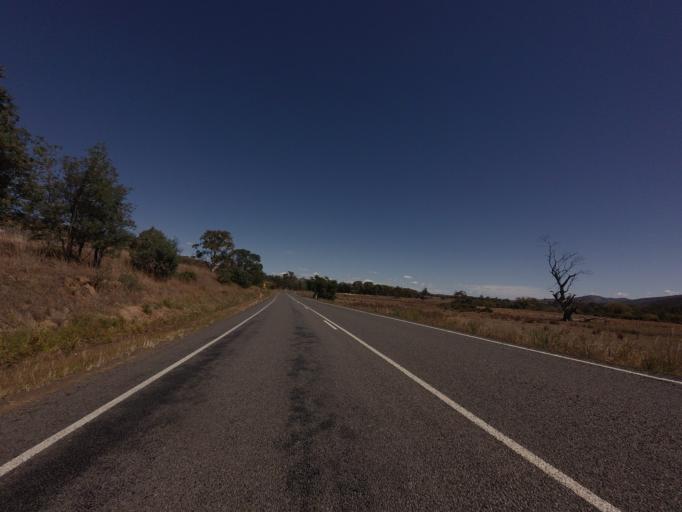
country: AU
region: Tasmania
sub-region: Northern Midlands
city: Evandale
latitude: -41.7477
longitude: 147.7821
